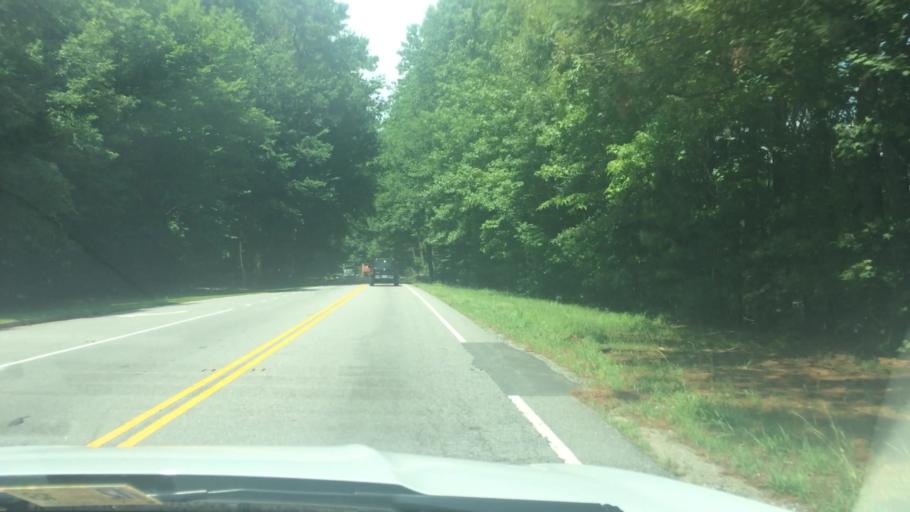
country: US
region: Virginia
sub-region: York County
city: Yorktown
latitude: 37.2044
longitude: -76.5816
